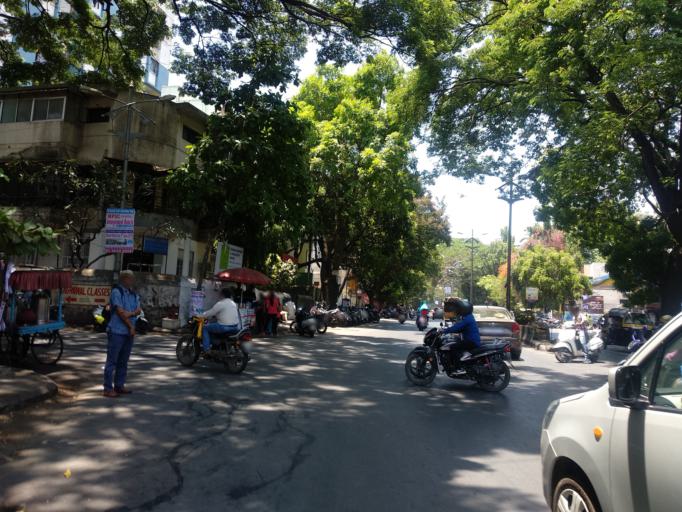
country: IN
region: Maharashtra
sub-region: Pune Division
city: Pune
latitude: 18.5084
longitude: 73.8441
